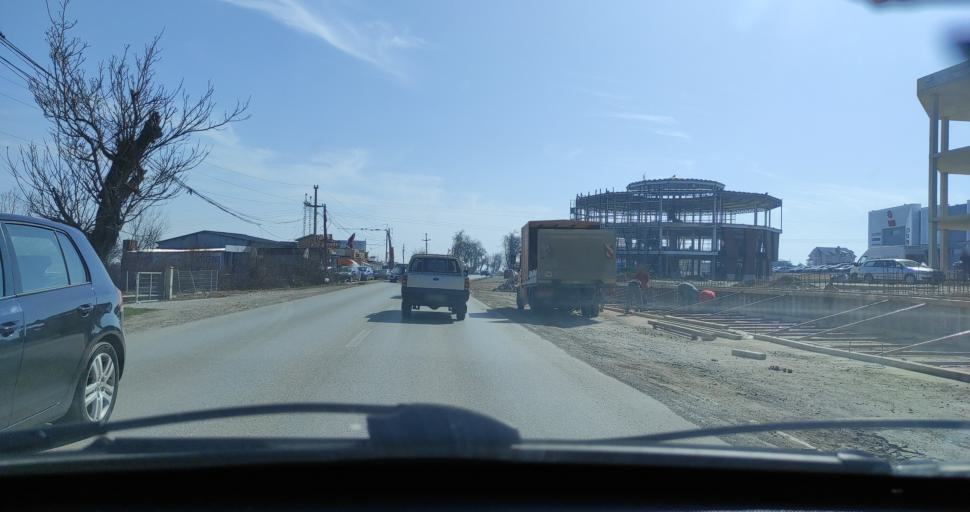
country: XK
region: Pec
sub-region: Komuna e Pejes
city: Peje
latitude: 42.6348
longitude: 20.3013
